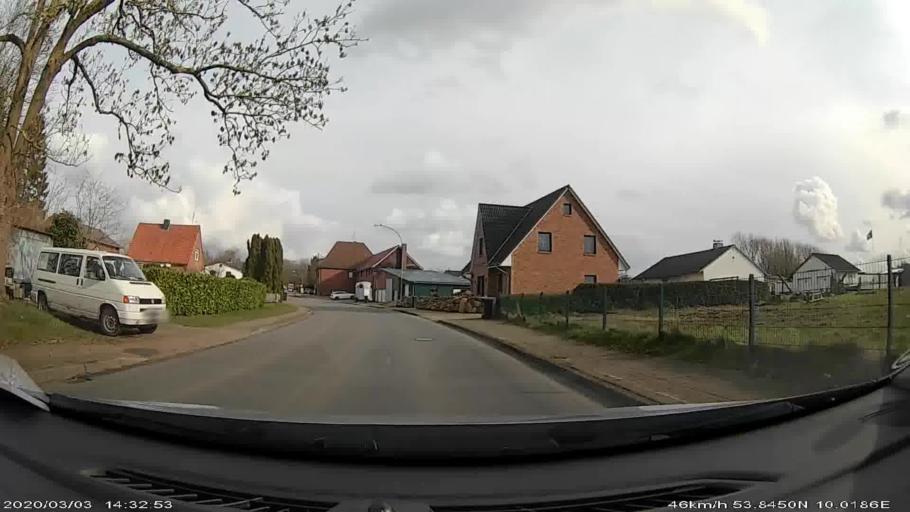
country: DE
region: Schleswig-Holstein
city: Kattendorf
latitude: 53.8451
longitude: 10.0192
